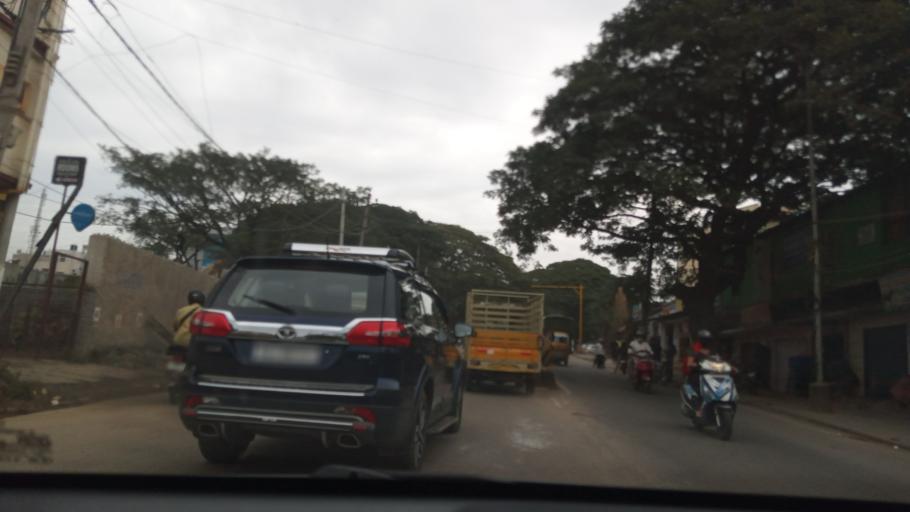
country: IN
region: Karnataka
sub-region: Bangalore Urban
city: Bangalore
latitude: 13.0194
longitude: 77.5391
